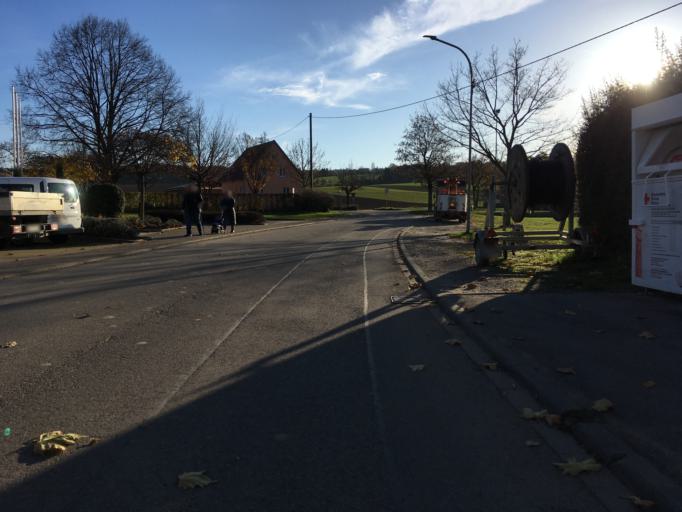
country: DE
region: Baden-Wuerttemberg
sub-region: Regierungsbezirk Stuttgart
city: Ilsfeld
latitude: 49.0526
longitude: 9.2422
